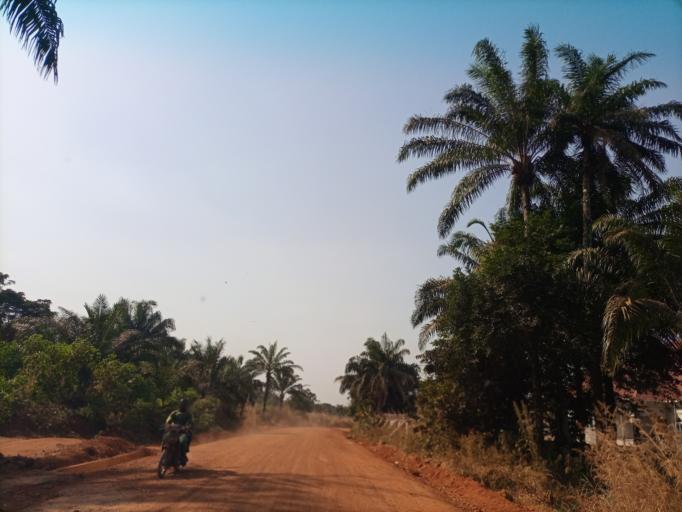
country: NG
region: Enugu
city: Aku
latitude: 6.7025
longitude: 7.3161
